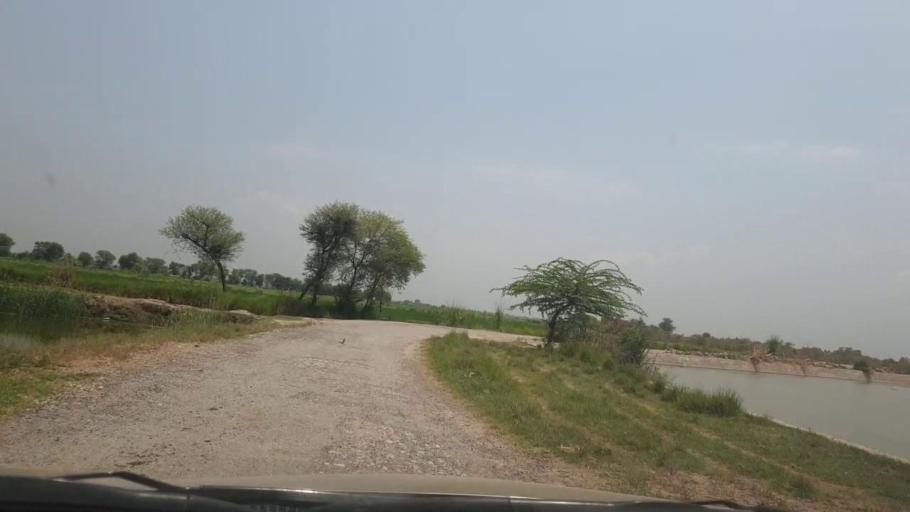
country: PK
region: Sindh
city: Ratodero
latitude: 27.7335
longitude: 68.3076
